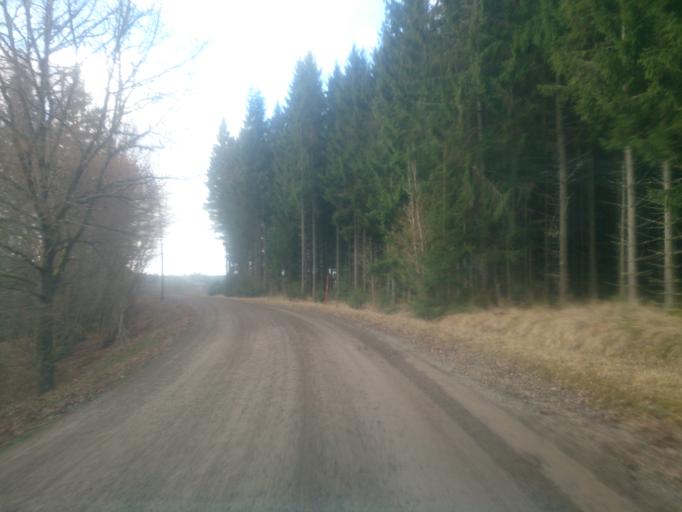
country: SE
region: OEstergoetland
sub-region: Atvidabergs Kommun
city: Atvidaberg
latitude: 58.1867
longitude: 16.1452
